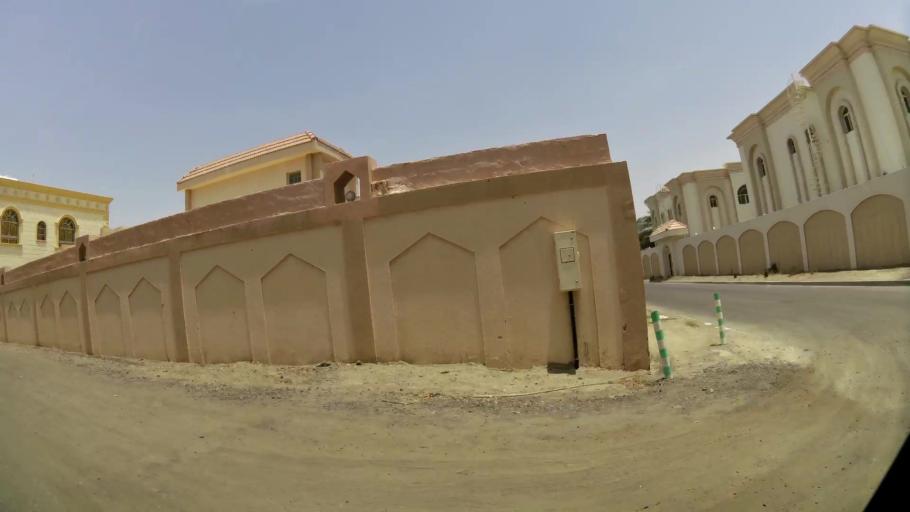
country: AE
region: Abu Dhabi
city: Al Ain
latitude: 24.1986
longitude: 55.7797
